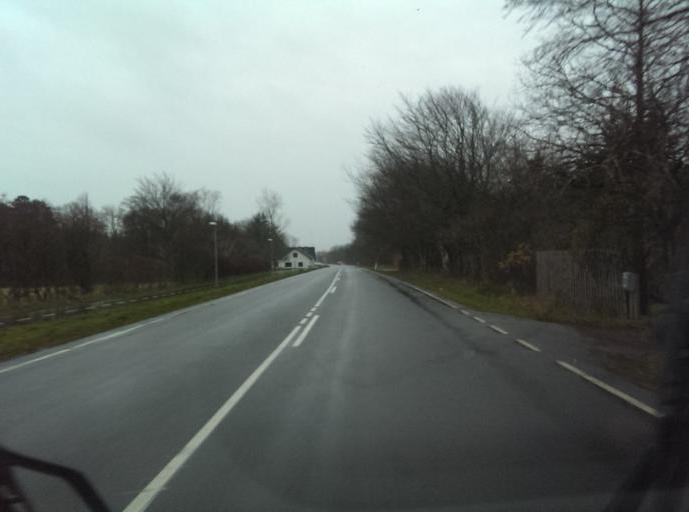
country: DK
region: South Denmark
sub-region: Esbjerg Kommune
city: Tjaereborg
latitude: 55.4905
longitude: 8.5169
